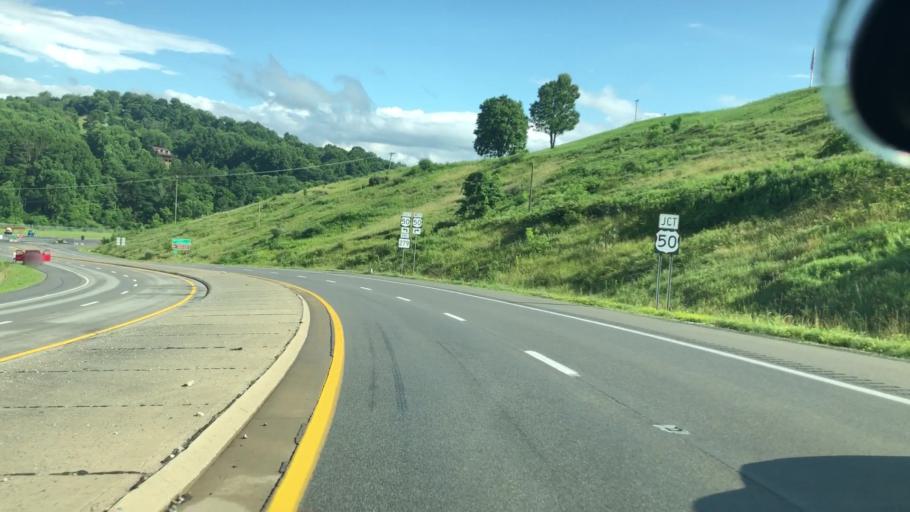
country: US
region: West Virginia
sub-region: Harrison County
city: Bridgeport
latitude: 39.2995
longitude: -80.2066
